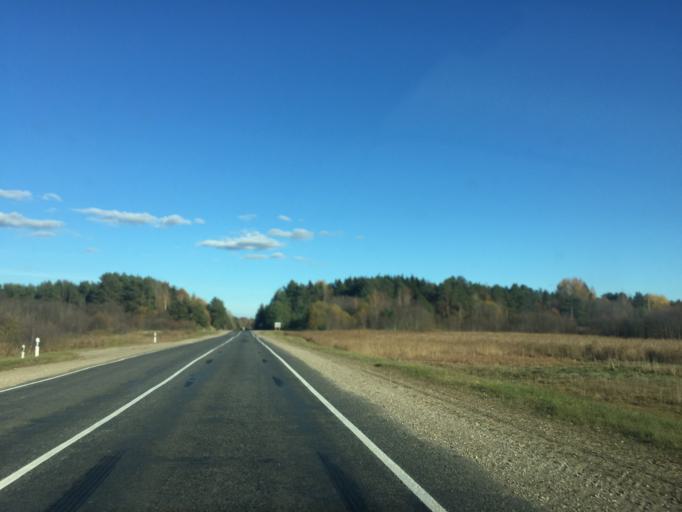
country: BY
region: Vitebsk
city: Dzisna
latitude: 55.2458
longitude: 28.0862
